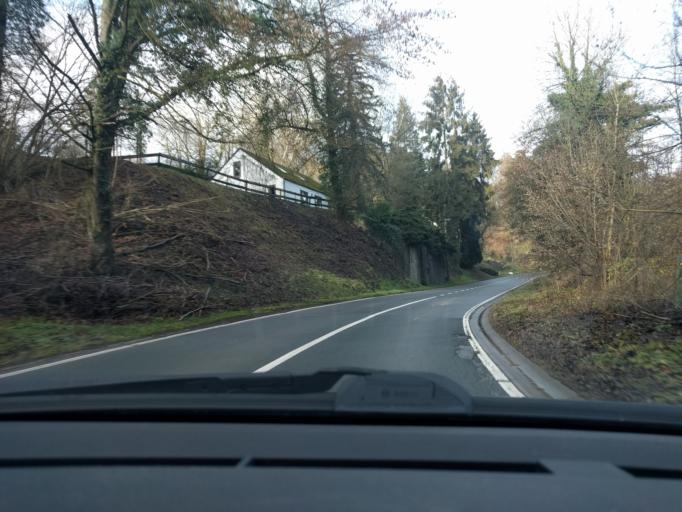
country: BE
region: Wallonia
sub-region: Province de Namur
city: Noville-les-Bois
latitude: 50.5022
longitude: 4.9533
